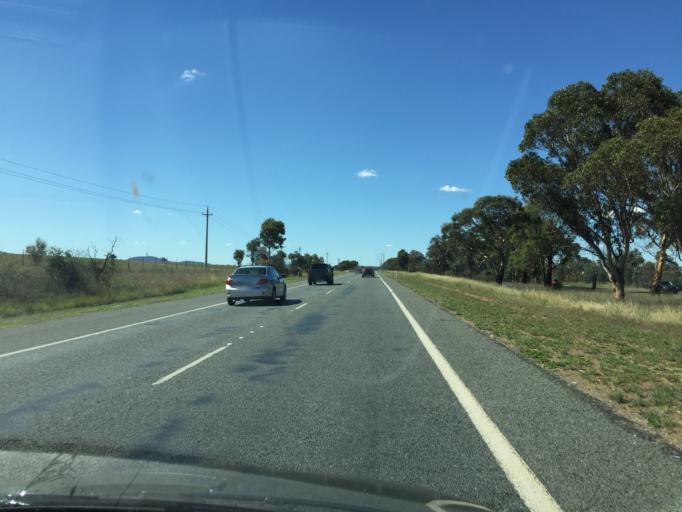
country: AU
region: Australian Capital Territory
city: Macarthur
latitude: -35.3771
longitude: 149.1693
